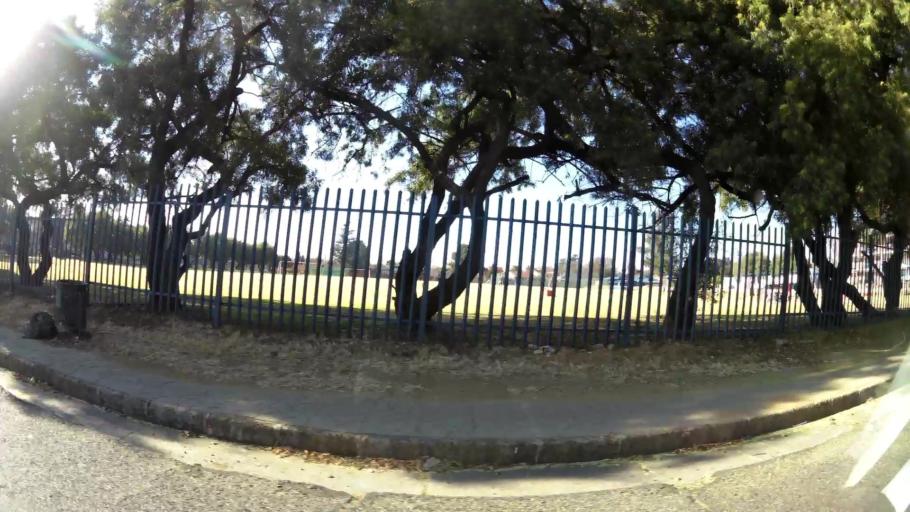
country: ZA
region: Gauteng
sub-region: City of Johannesburg Metropolitan Municipality
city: Modderfontein
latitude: -26.1336
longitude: 28.1567
